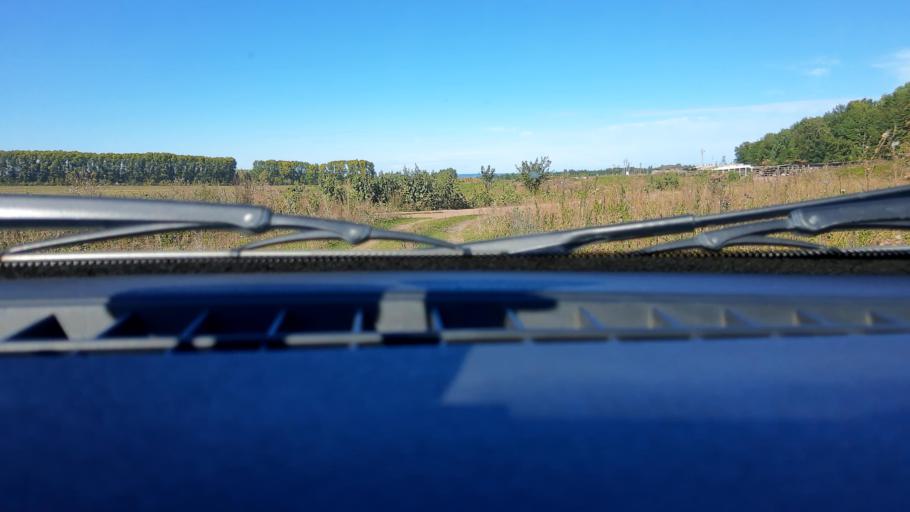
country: RU
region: Bashkortostan
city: Asanovo
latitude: 54.8160
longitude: 55.6217
